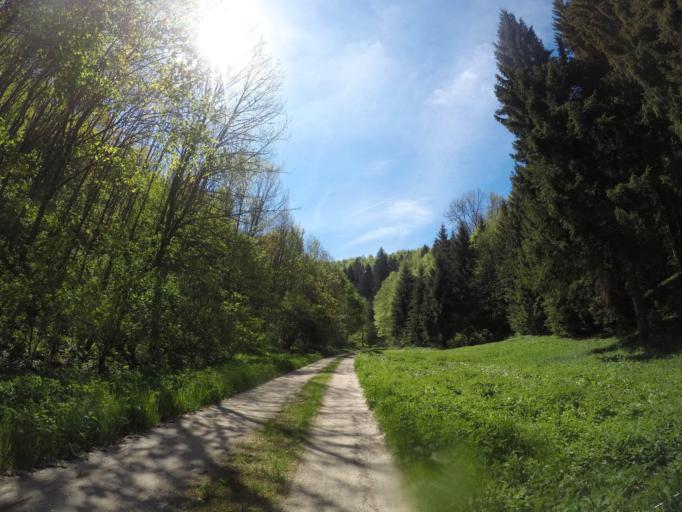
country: DE
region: Baden-Wuerttemberg
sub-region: Tuebingen Region
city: Laichingen
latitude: 48.4290
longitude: 9.6833
